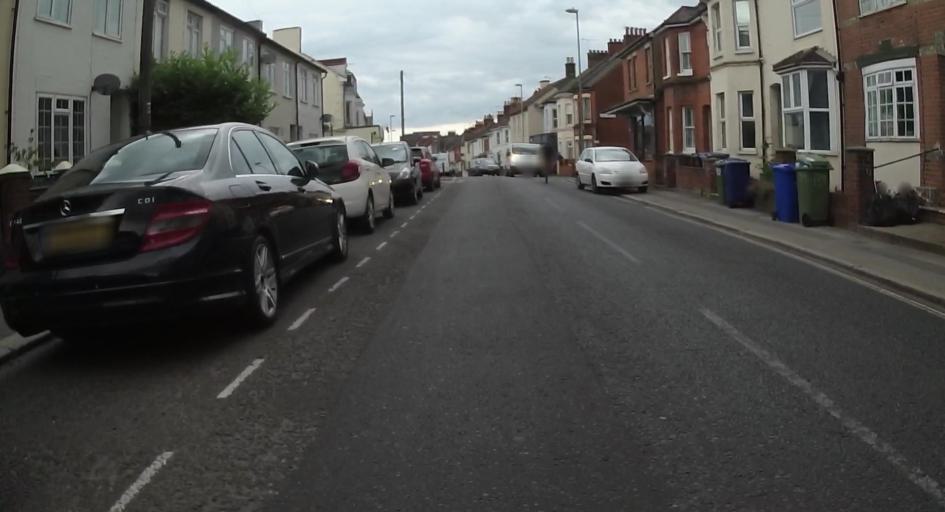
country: GB
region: England
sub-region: Hampshire
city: Aldershot
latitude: 51.2458
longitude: -0.7657
